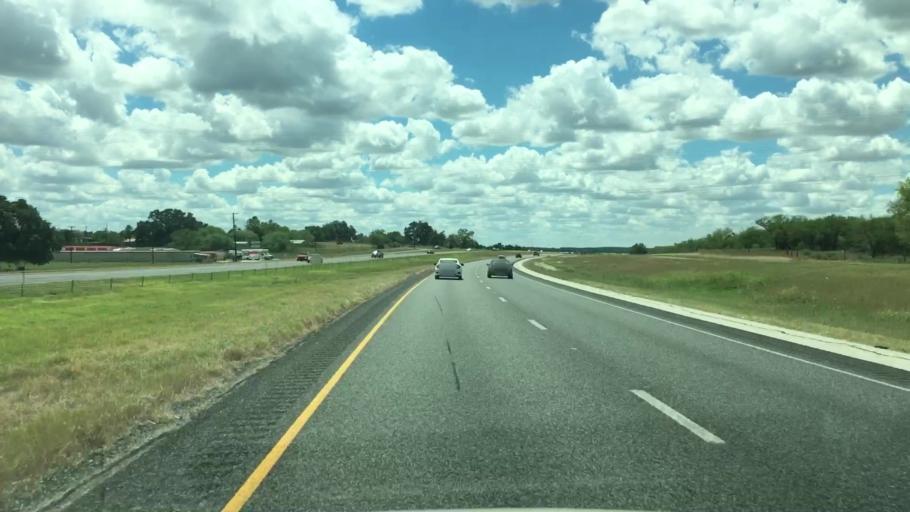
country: US
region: Texas
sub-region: Bexar County
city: Elmendorf
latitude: 29.2489
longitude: -98.3957
